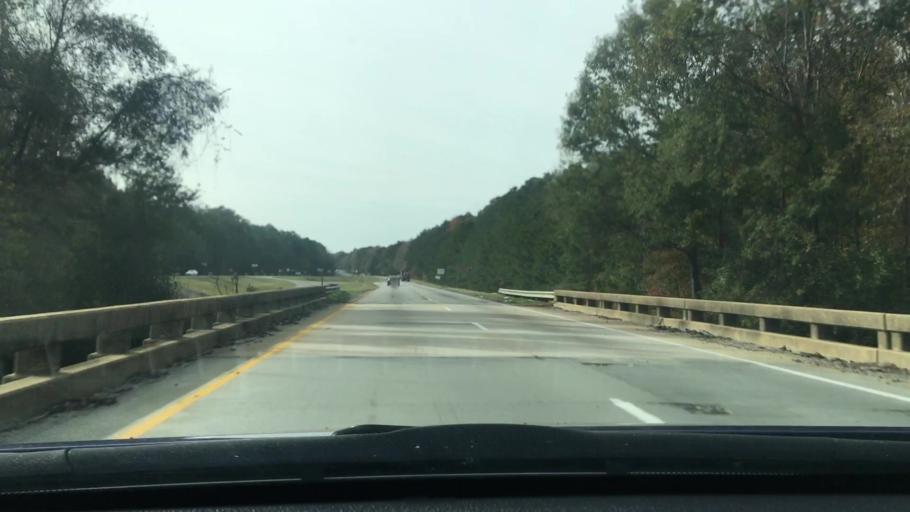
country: US
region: South Carolina
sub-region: Sumter County
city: Stateburg
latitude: 33.9473
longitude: -80.6306
